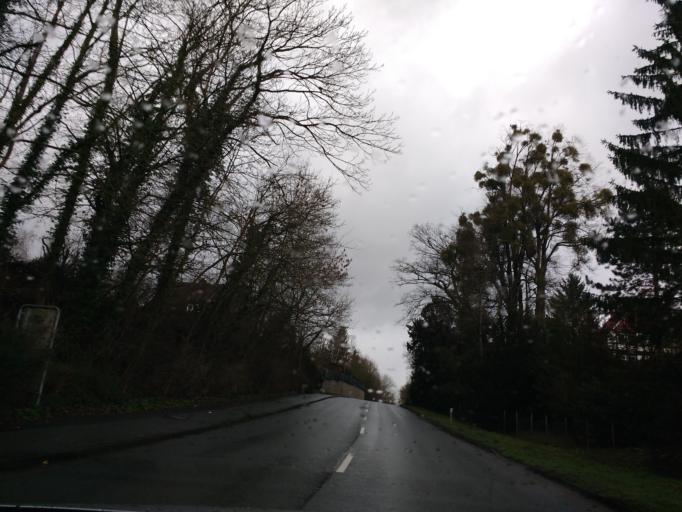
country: DE
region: Lower Saxony
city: Hessisch Oldendorf
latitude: 52.1723
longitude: 9.2529
